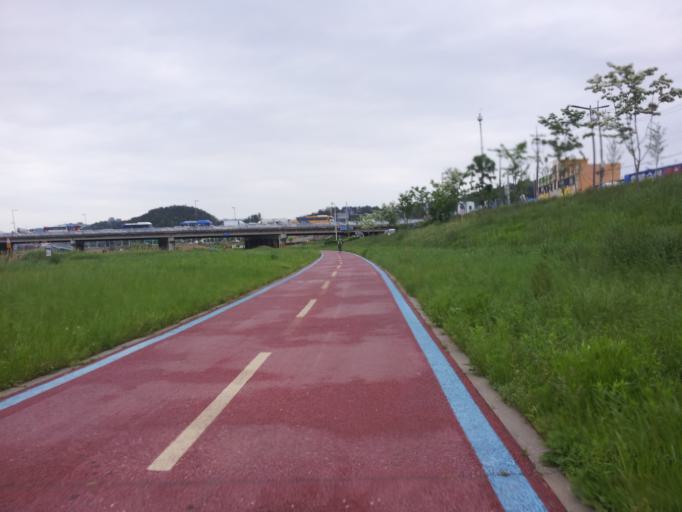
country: KR
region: Daejeon
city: Daejeon
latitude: 36.3551
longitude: 127.4050
